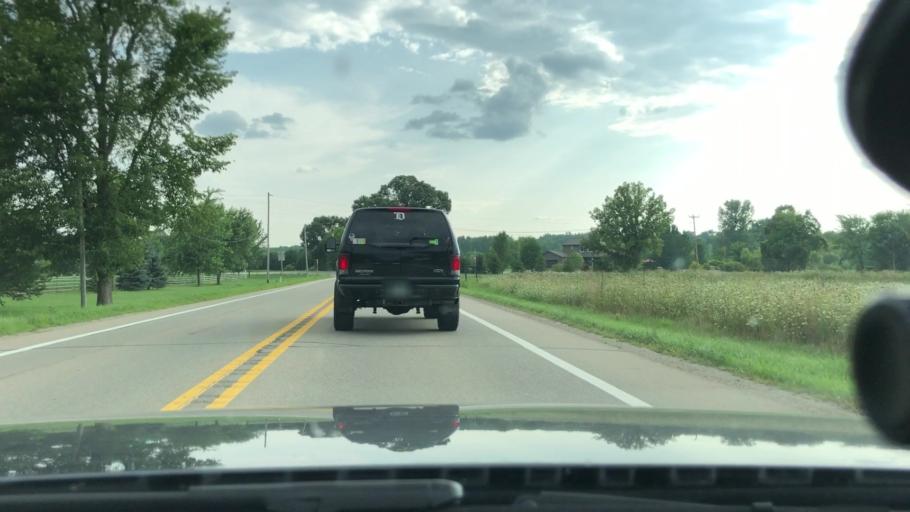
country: US
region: Michigan
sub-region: Washtenaw County
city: Chelsea
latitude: 42.2449
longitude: -84.0355
